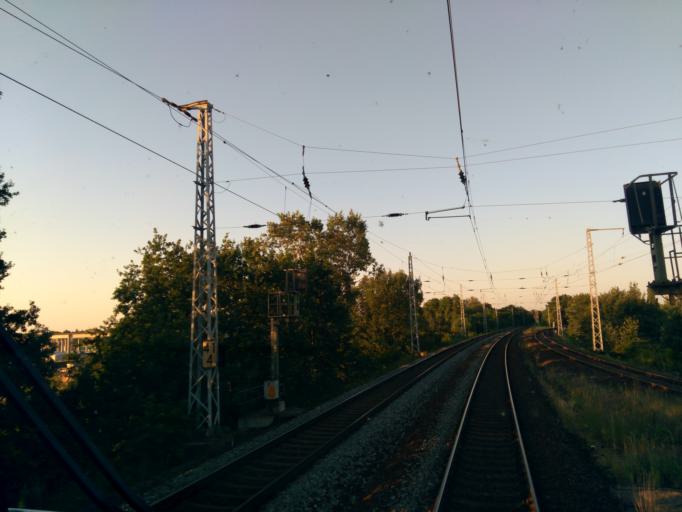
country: DE
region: Berlin
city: Adlershof
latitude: 52.4323
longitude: 13.5633
